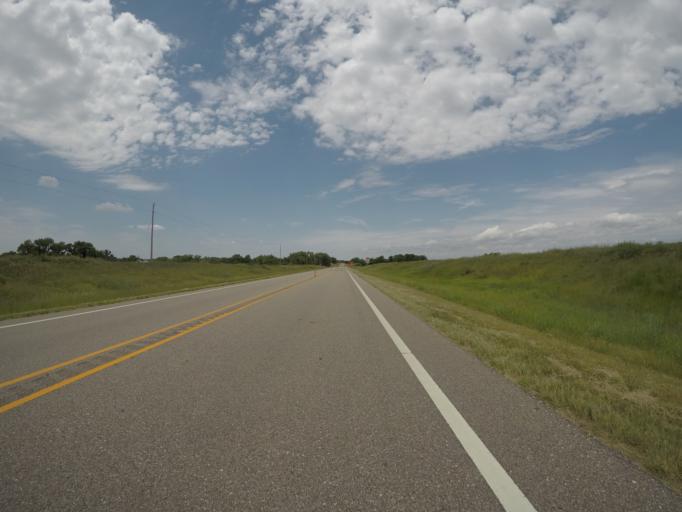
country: US
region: Kansas
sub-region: Graham County
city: Hill City
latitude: 39.3944
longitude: -99.6289
